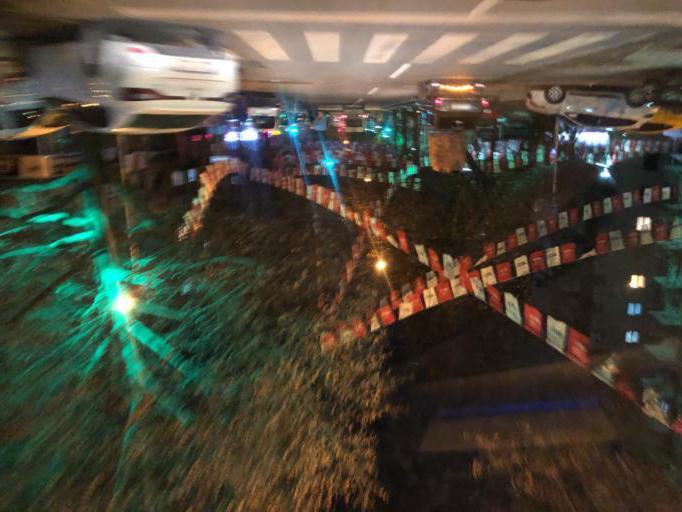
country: TR
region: Ankara
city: Batikent
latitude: 39.9679
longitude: 32.7871
